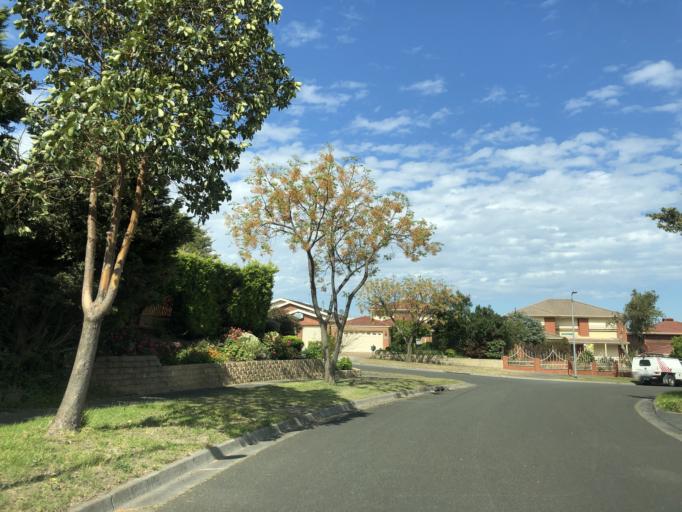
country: AU
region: Victoria
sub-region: Casey
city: Endeavour Hills
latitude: -37.9827
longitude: 145.2757
